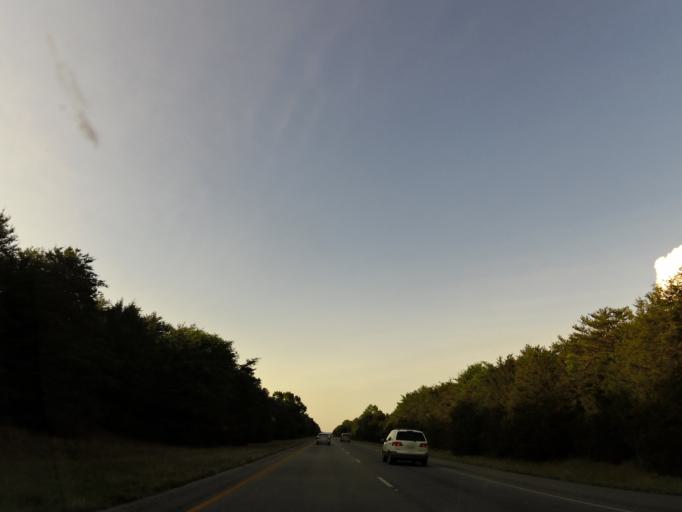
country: US
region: Georgia
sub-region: Dade County
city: Trenton
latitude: 34.8412
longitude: -85.5320
